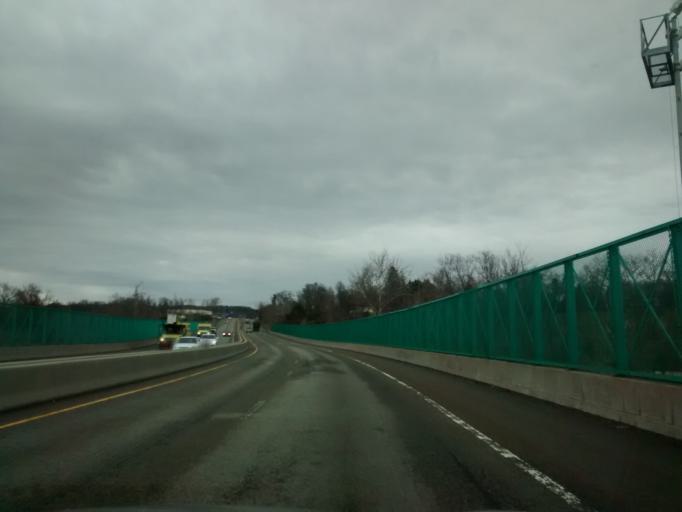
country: US
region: Massachusetts
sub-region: Worcester County
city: Millbury
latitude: 42.2123
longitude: -71.7845
